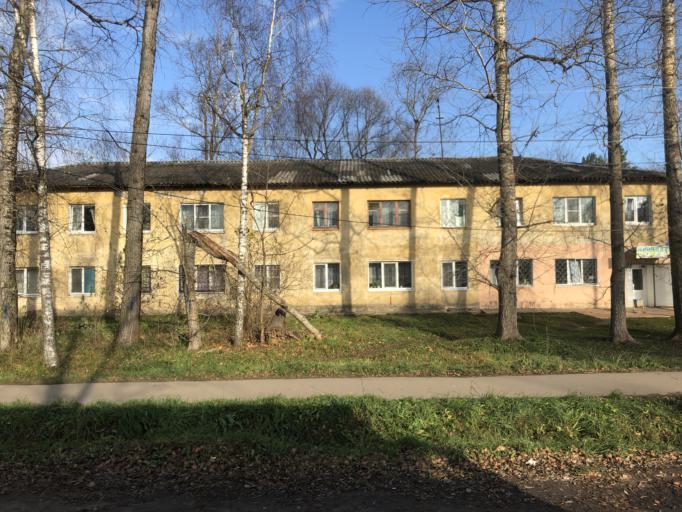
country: RU
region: Tverskaya
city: Rzhev
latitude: 56.2635
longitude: 34.3109
